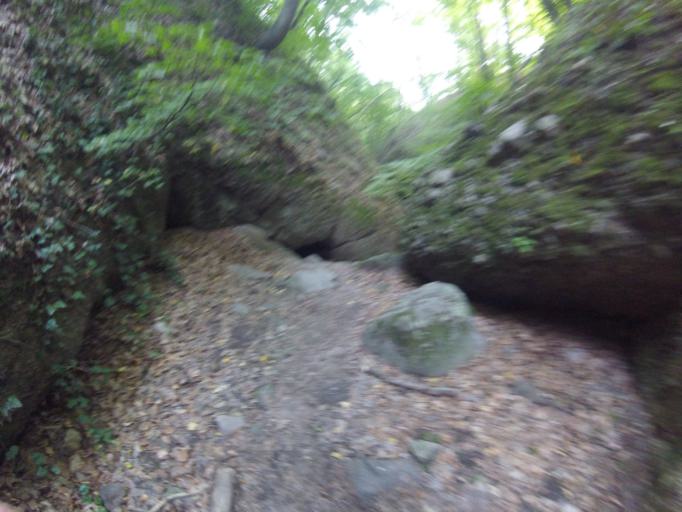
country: HU
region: Pest
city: Csobanka
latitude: 47.6760
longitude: 18.9746
